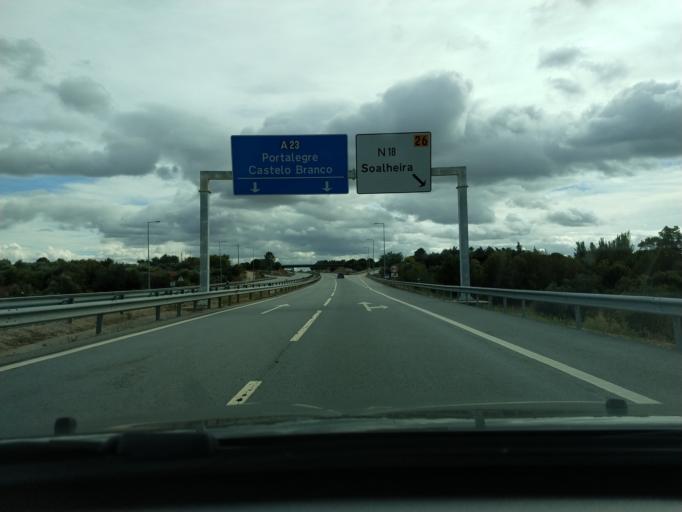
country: PT
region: Castelo Branco
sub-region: Concelho do Fundao
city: Fundao
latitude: 40.0321
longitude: -7.4684
